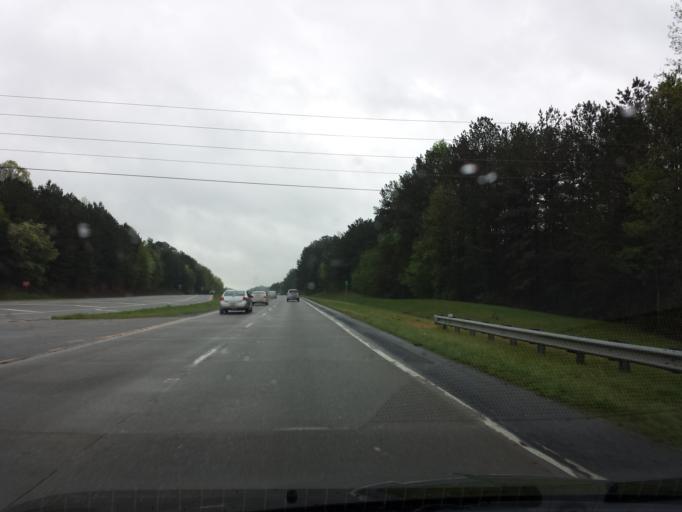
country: US
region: Georgia
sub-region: Pickens County
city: Nelson
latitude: 34.3909
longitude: -84.4061
